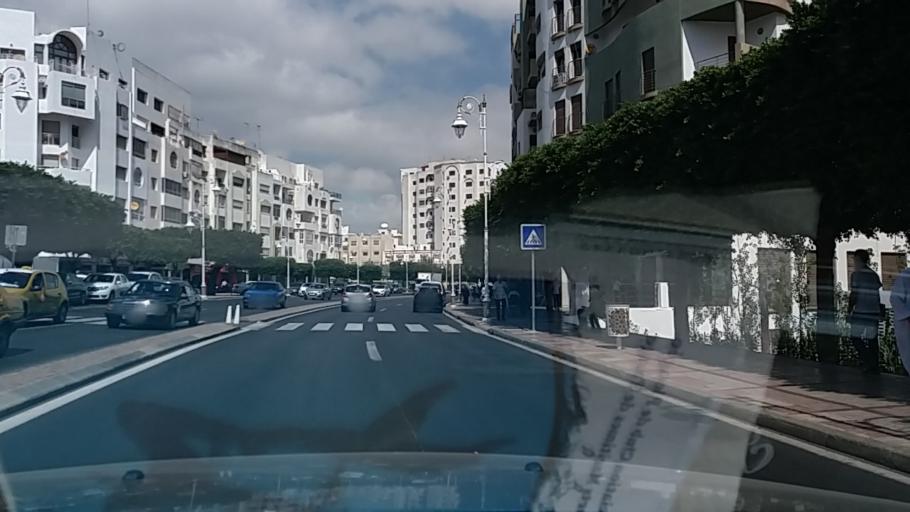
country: MA
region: Tanger-Tetouan
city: Tetouan
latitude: 35.5735
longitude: -5.3601
